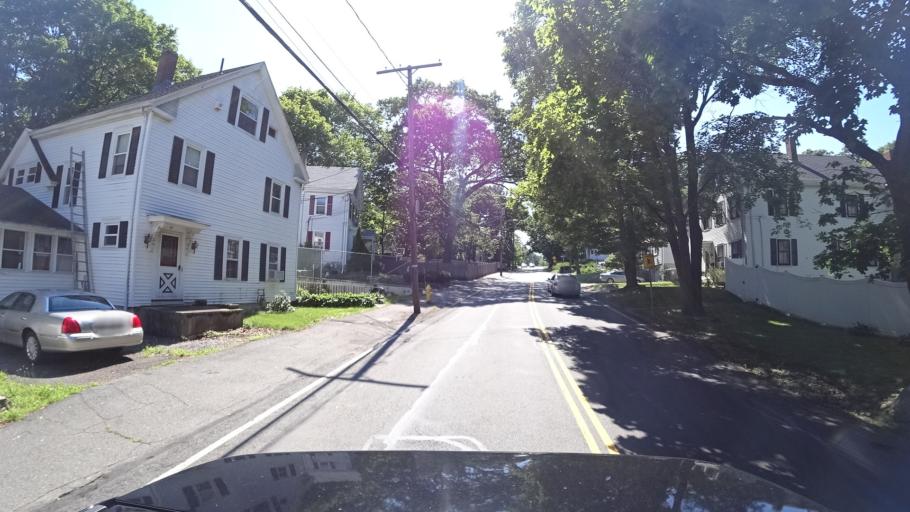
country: US
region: Massachusetts
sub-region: Norfolk County
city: Dedham
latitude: 42.2413
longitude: -71.1521
